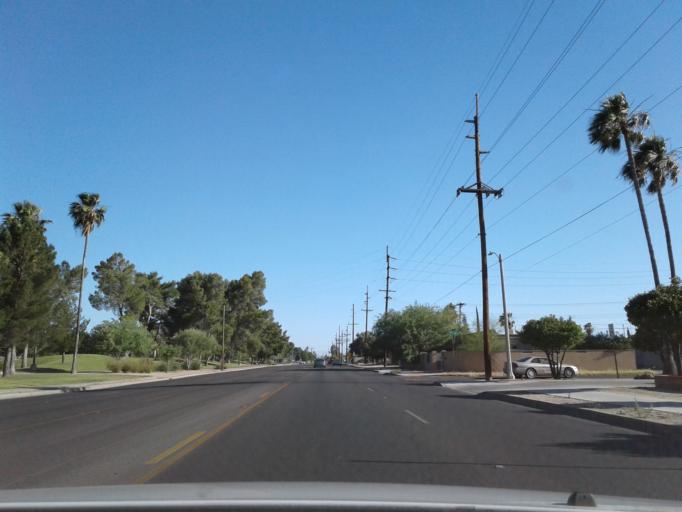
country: US
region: Arizona
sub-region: Pima County
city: Tucson
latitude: 32.2111
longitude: -110.9267
